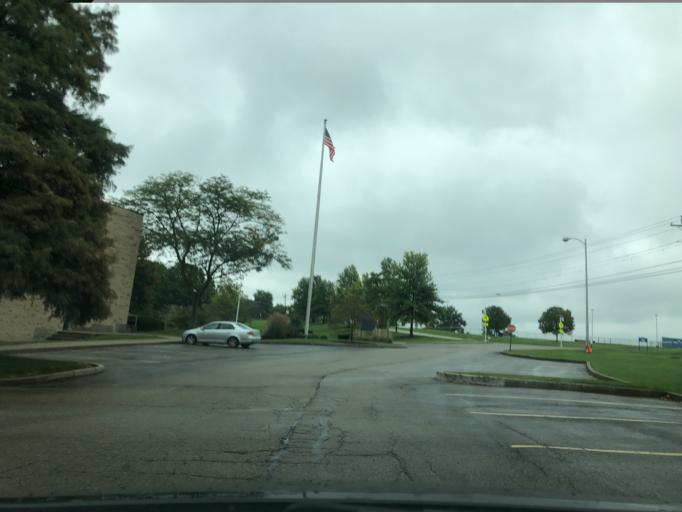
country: US
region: Ohio
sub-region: Hamilton County
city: Finneytown
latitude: 39.2079
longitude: -84.5051
